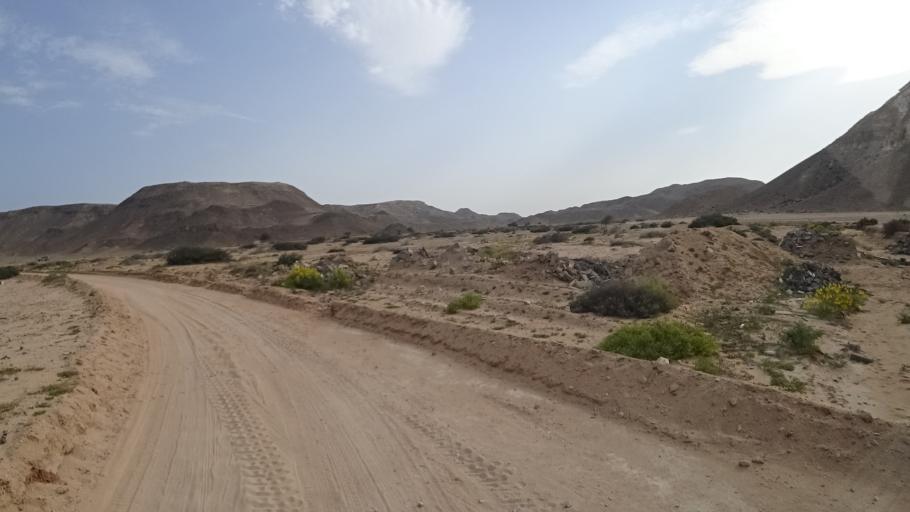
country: OM
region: Ash Sharqiyah
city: Sur
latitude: 22.4371
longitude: 59.8175
